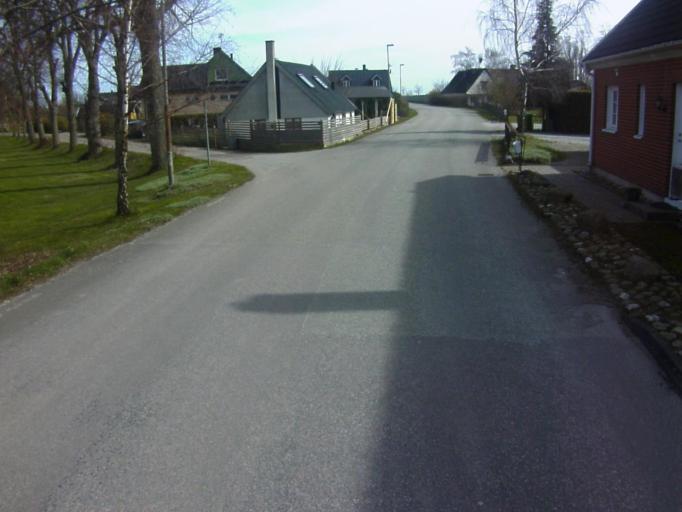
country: SE
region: Skane
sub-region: Kavlinge Kommun
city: Kaevlinge
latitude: 55.7740
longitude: 13.1123
